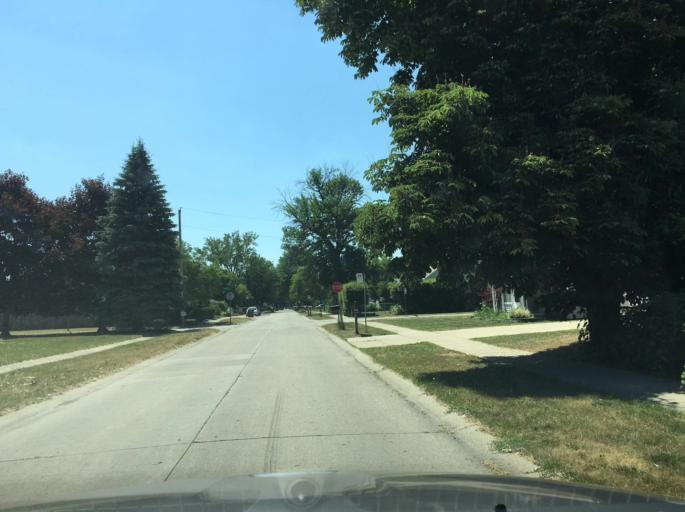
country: US
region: Michigan
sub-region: Macomb County
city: Fraser
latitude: 42.5443
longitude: -82.9129
